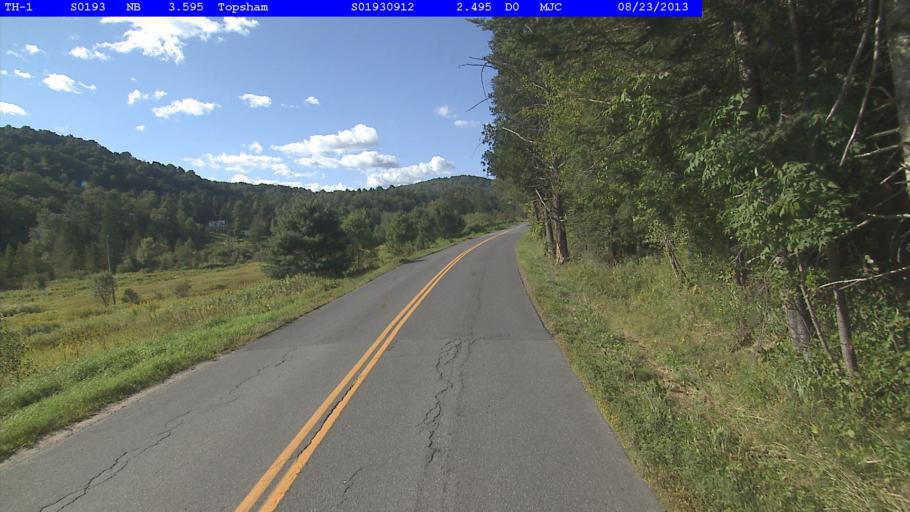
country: US
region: New Hampshire
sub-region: Grafton County
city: Haverhill
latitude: 44.1035
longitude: -72.2314
